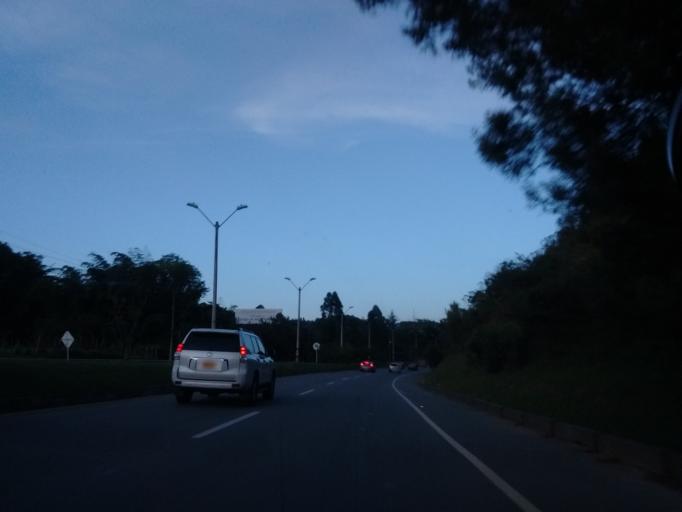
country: CO
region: Antioquia
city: Santuario
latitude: 6.1372
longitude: -75.2826
